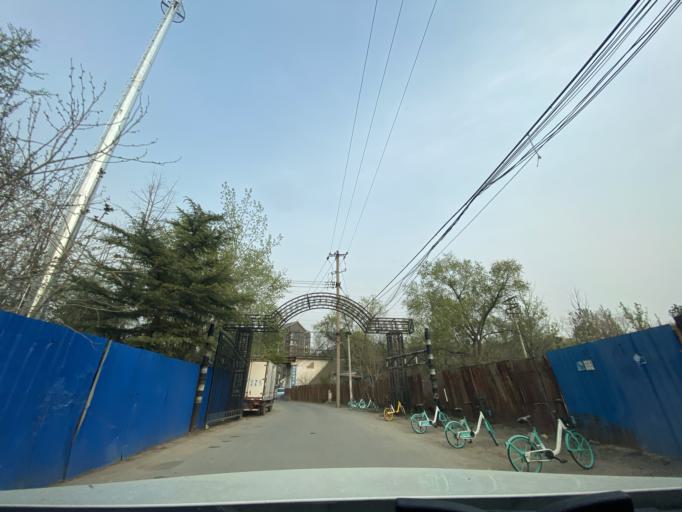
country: CN
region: Beijing
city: Babaoshan
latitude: 39.9326
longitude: 116.2313
